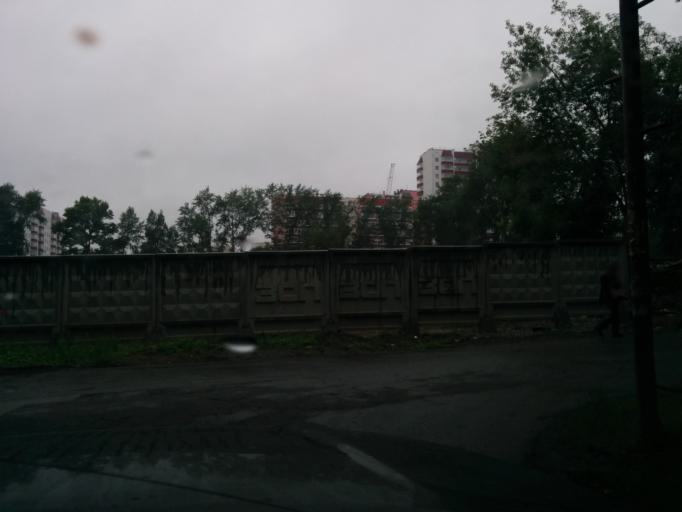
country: RU
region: Perm
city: Kondratovo
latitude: 58.0333
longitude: 56.0314
